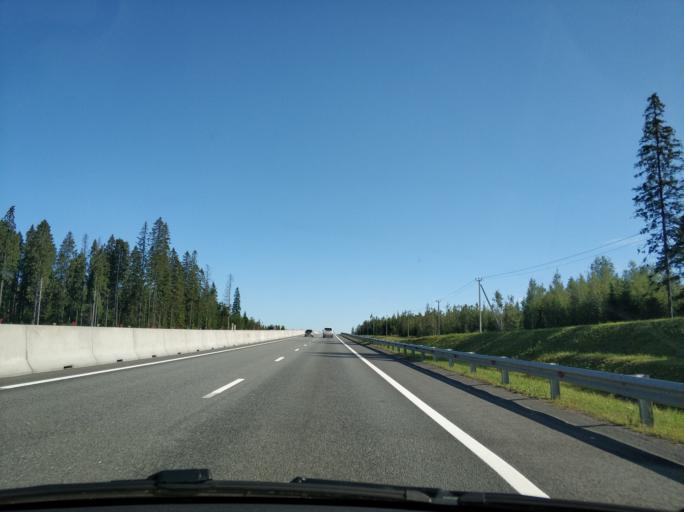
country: RU
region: Leningrad
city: Sosnovo
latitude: 60.4648
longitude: 30.1962
